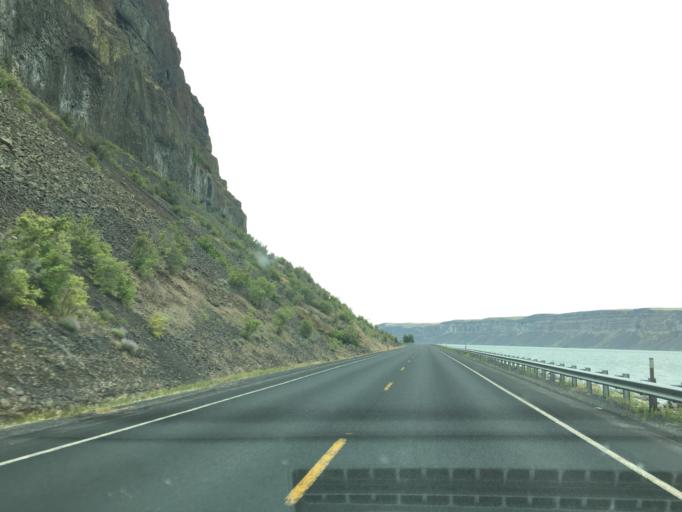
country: US
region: Washington
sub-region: Okanogan County
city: Coulee Dam
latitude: 47.8021
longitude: -119.1801
